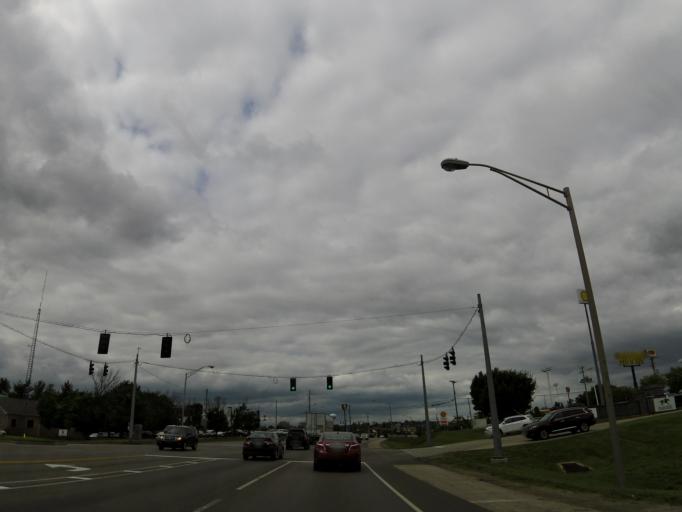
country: US
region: Kentucky
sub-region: Scott County
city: Georgetown
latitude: 38.2184
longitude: -84.5410
